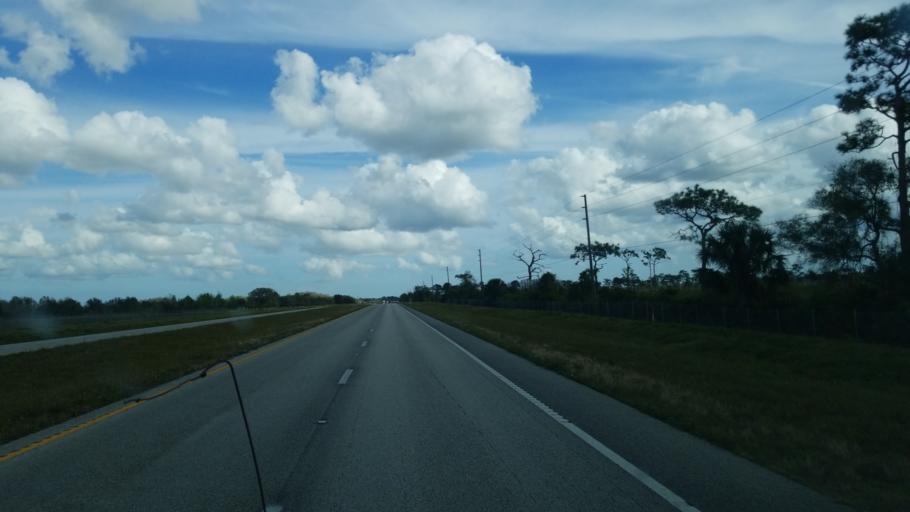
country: US
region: Florida
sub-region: Osceola County
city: Saint Cloud
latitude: 28.1299
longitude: -80.9987
